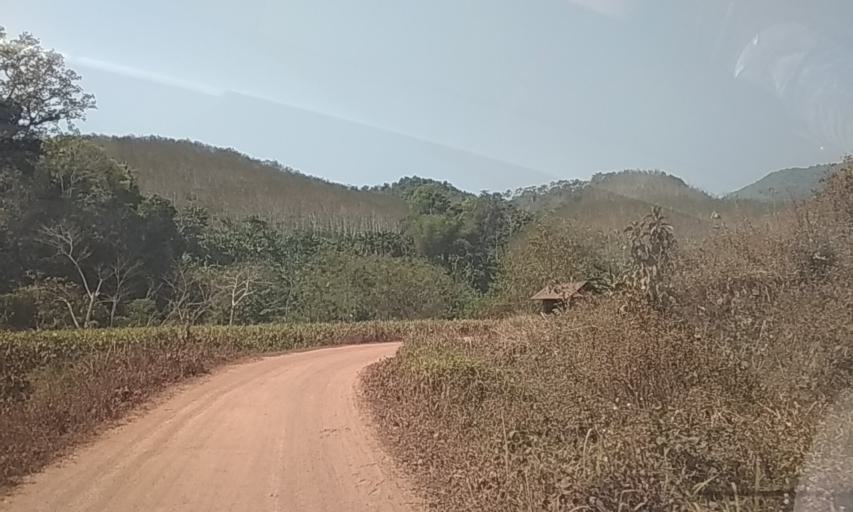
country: CN
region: Yunnan
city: Mengla
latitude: 21.5258
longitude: 101.8350
